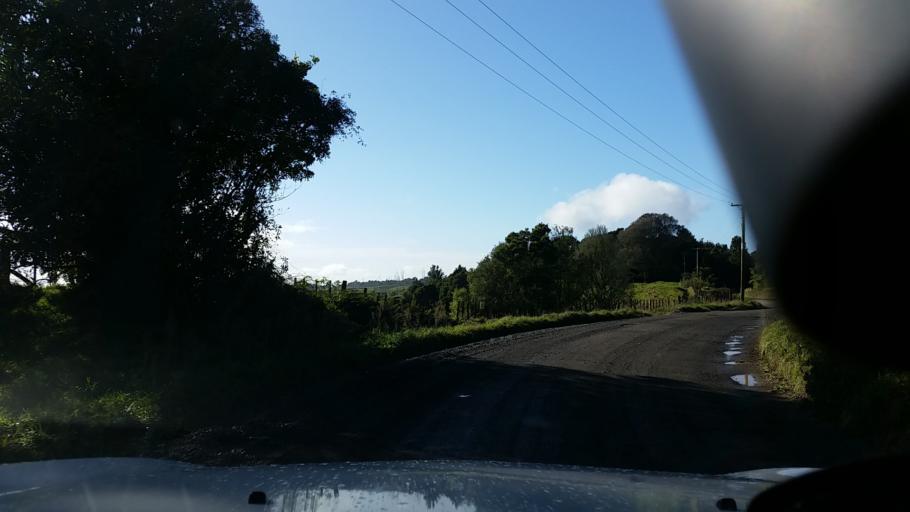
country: NZ
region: Bay of Plenty
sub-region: Kawerau District
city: Kawerau
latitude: -38.0182
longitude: 176.4660
